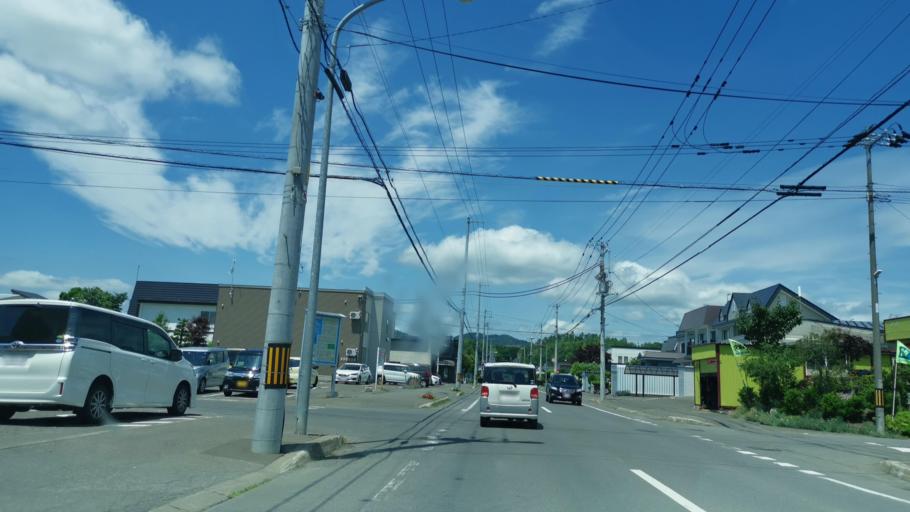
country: JP
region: Hokkaido
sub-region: Asahikawa-shi
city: Asahikawa
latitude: 43.7939
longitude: 142.3333
